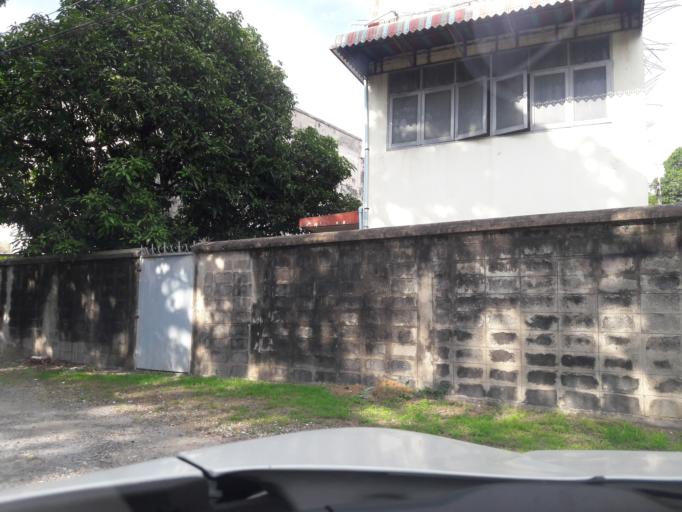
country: TH
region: Lop Buri
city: Ban Mi
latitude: 15.0416
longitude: 100.5391
